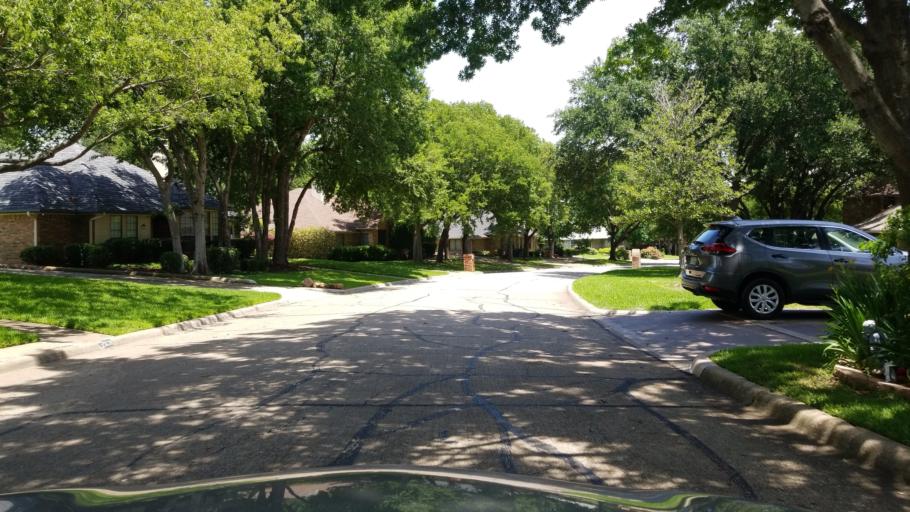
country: US
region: Texas
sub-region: Dallas County
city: Grand Prairie
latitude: 32.6861
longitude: -96.9867
